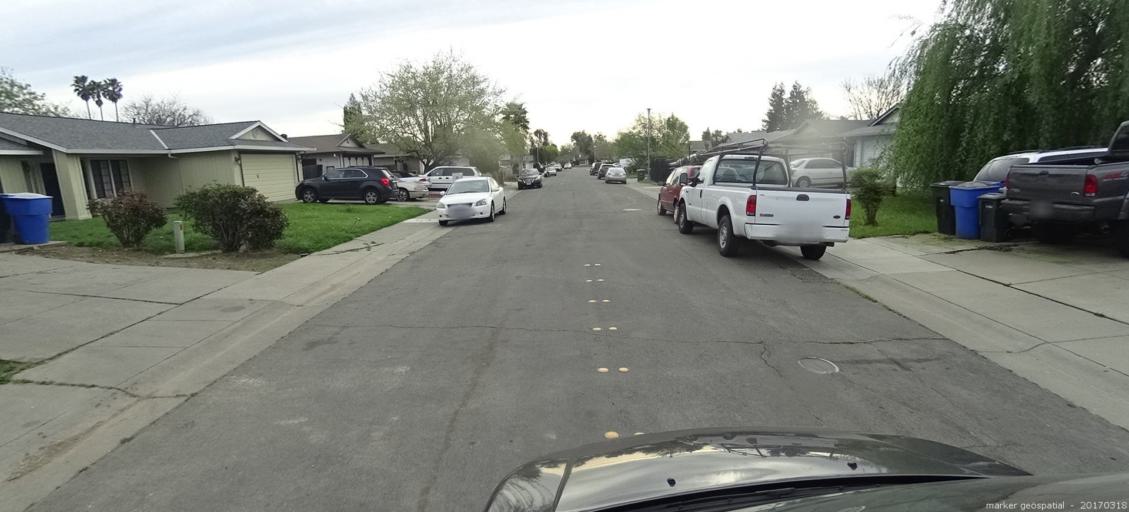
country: US
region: California
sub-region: Sacramento County
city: Parkway
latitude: 38.4846
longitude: -121.4631
